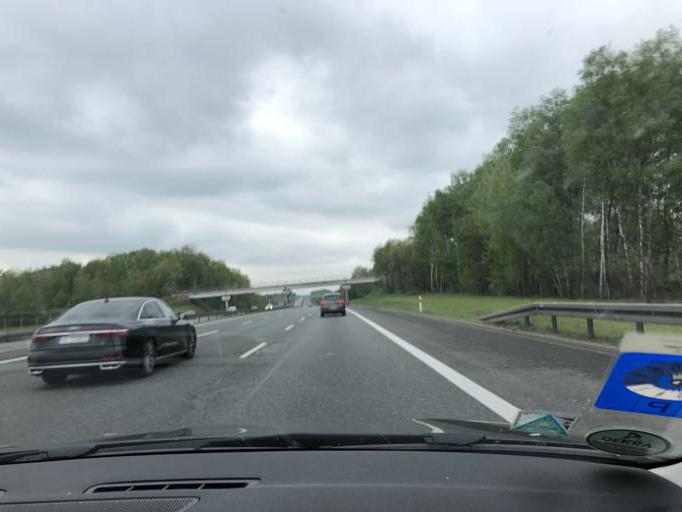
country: PL
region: Silesian Voivodeship
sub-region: Ruda Slaska
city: Ruda Slaska
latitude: 50.2587
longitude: 18.8337
